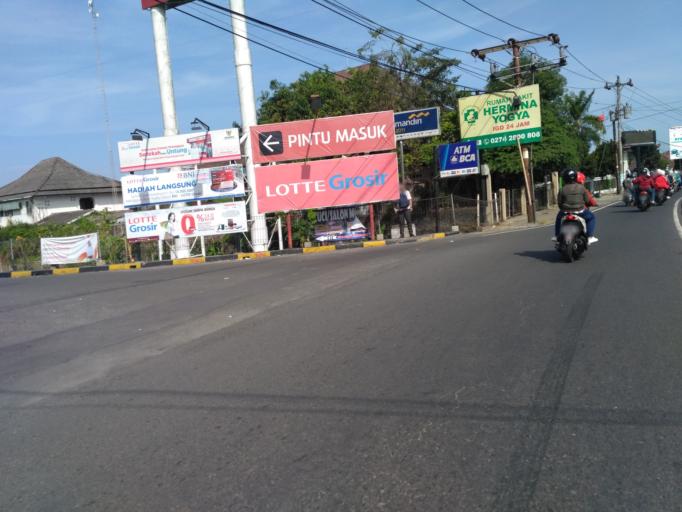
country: ID
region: Daerah Istimewa Yogyakarta
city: Depok
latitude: -7.7673
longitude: 110.4314
